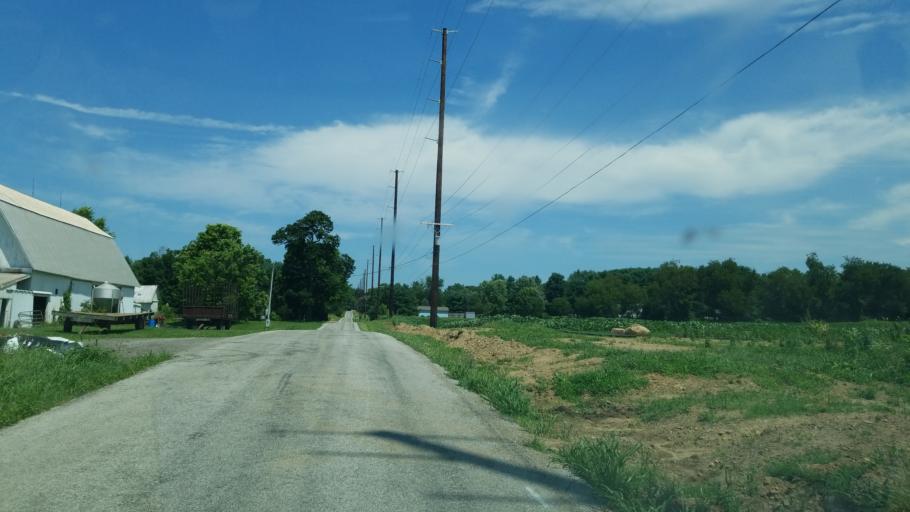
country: US
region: Ohio
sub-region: Ashland County
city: Ashland
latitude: 40.8847
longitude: -82.2690
